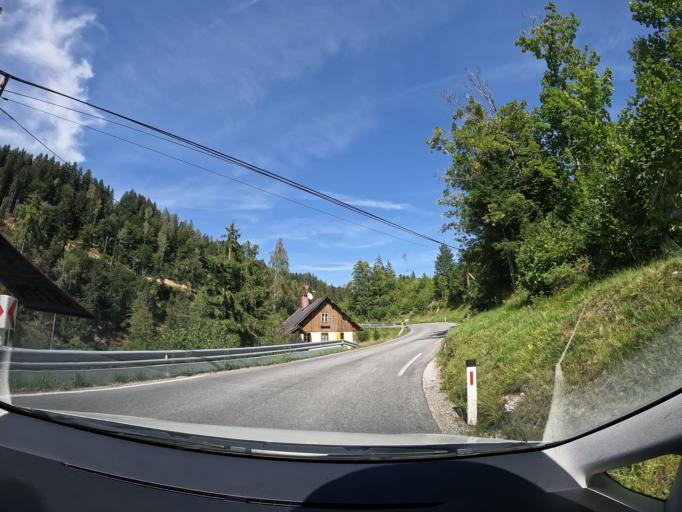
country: AT
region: Carinthia
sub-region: Politischer Bezirk Klagenfurt Land
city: Schiefling am See
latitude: 46.5892
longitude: 14.0699
